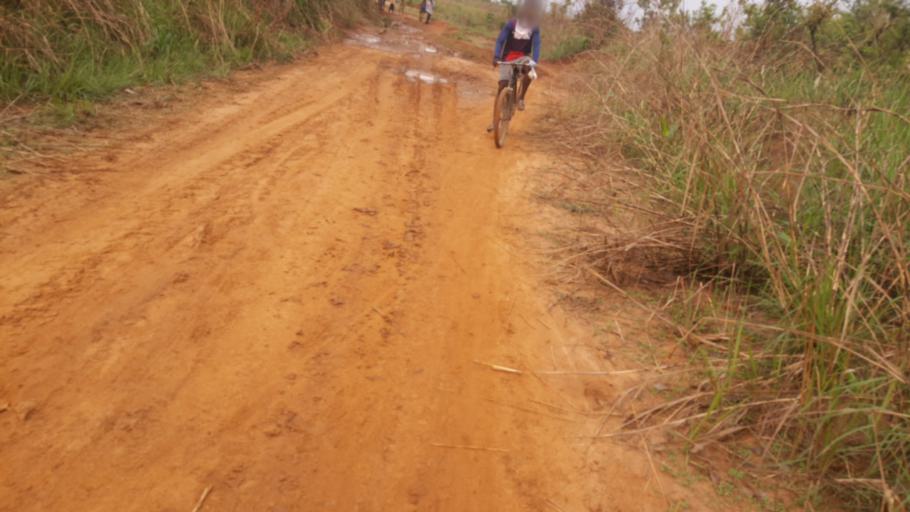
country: CD
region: Bandundu
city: Bandundu
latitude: -3.4631
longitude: 17.7171
